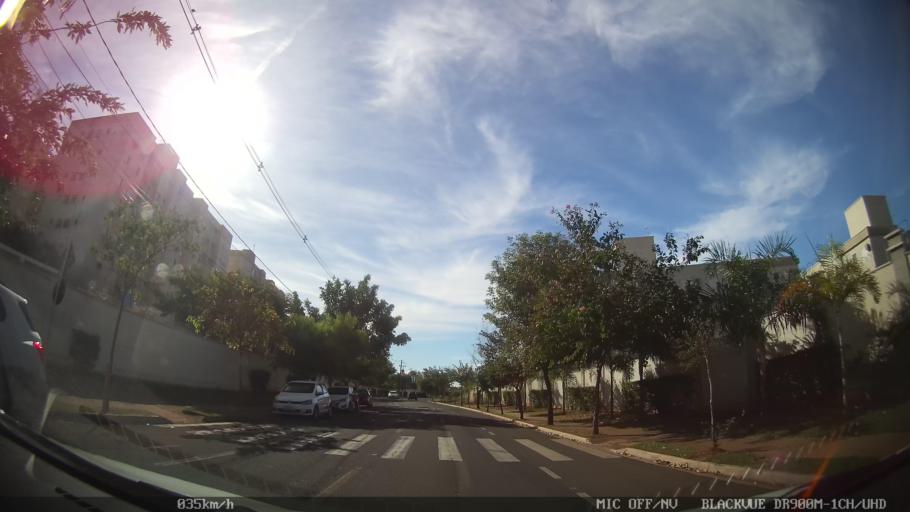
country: BR
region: Sao Paulo
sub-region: Sao Jose Do Rio Preto
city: Sao Jose do Rio Preto
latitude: -20.7869
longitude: -49.3501
